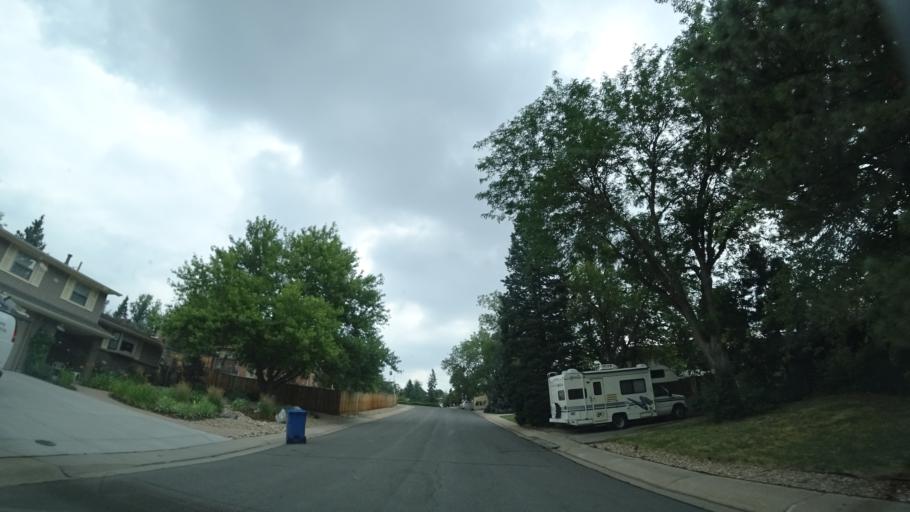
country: US
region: Colorado
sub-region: Jefferson County
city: West Pleasant View
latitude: 39.7033
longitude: -105.1498
